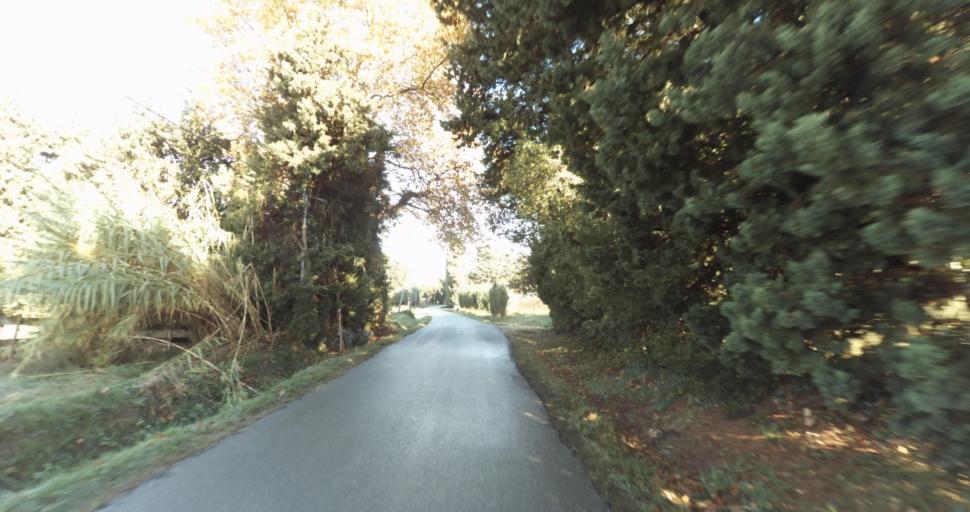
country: FR
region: Provence-Alpes-Cote d'Azur
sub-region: Departement des Bouches-du-Rhone
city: Rognonas
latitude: 43.8866
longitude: 4.7993
